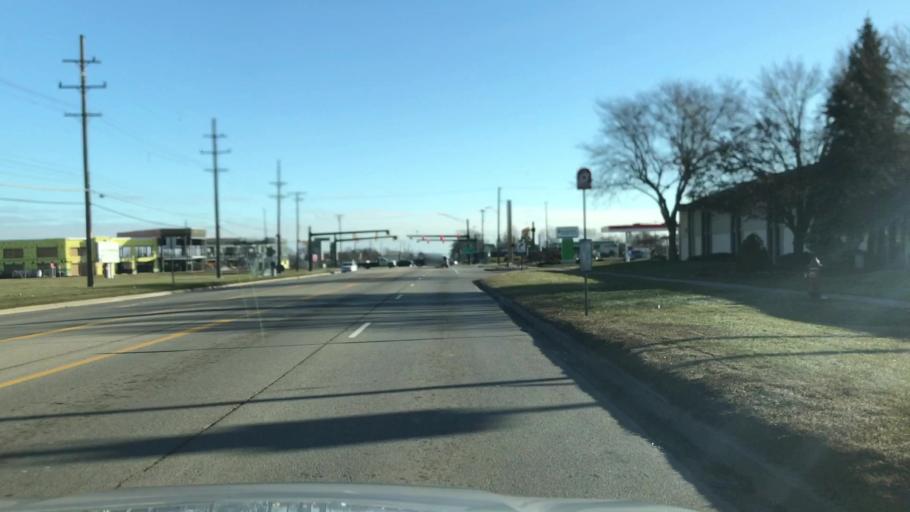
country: US
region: Michigan
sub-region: Macomb County
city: Sterling Heights
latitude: 42.5510
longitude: -83.0311
